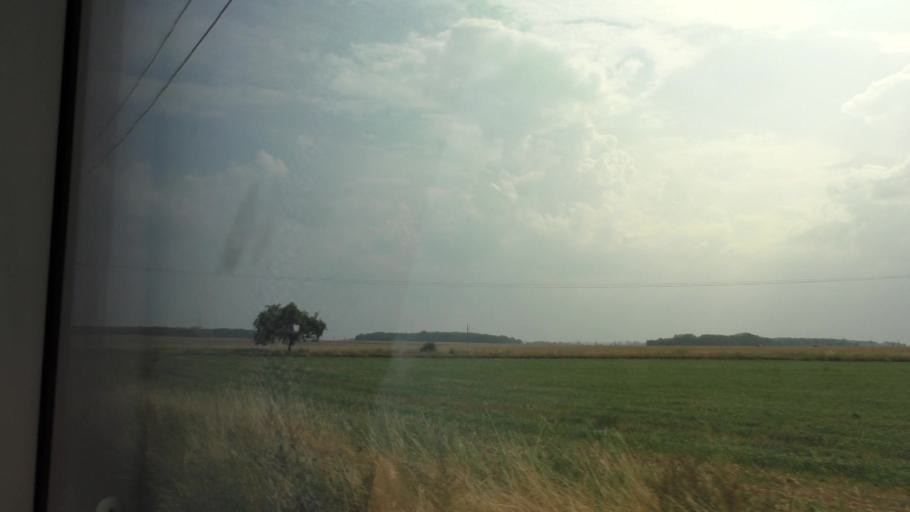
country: DE
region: Brandenburg
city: Rietz Neuendorf
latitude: 52.2013
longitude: 14.1346
